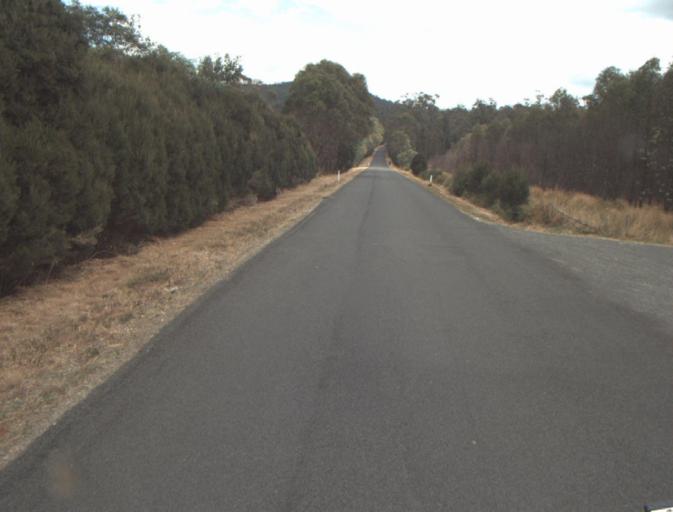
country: AU
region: Tasmania
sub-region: Launceston
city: Mayfield
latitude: -41.2119
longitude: 147.0563
